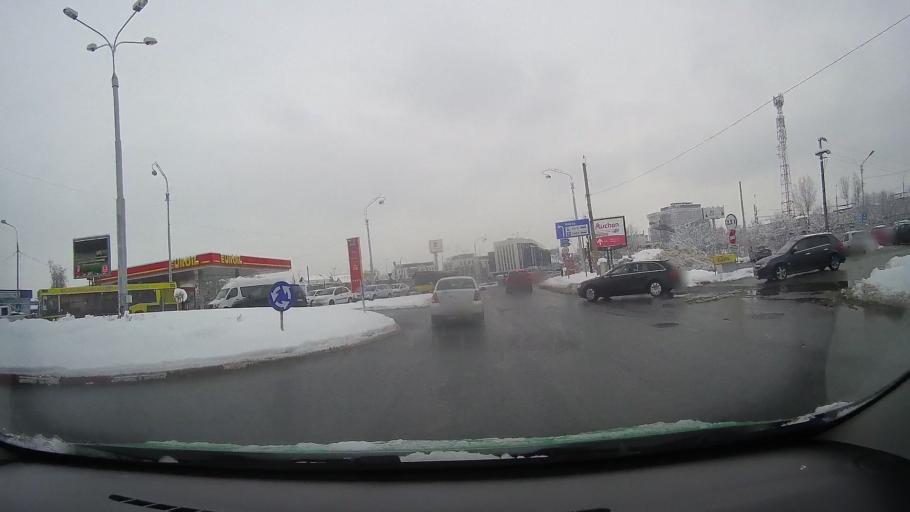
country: RO
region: Sibiu
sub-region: Municipiul Sibiu
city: Sibiu
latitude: 45.7934
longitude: 24.1308
